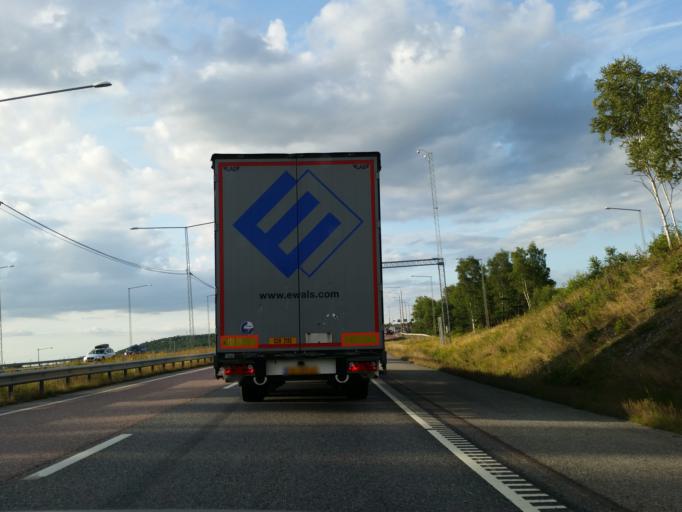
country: SE
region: Stockholm
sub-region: Sodertalje Kommun
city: Soedertaelje
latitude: 59.1800
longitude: 17.6420
